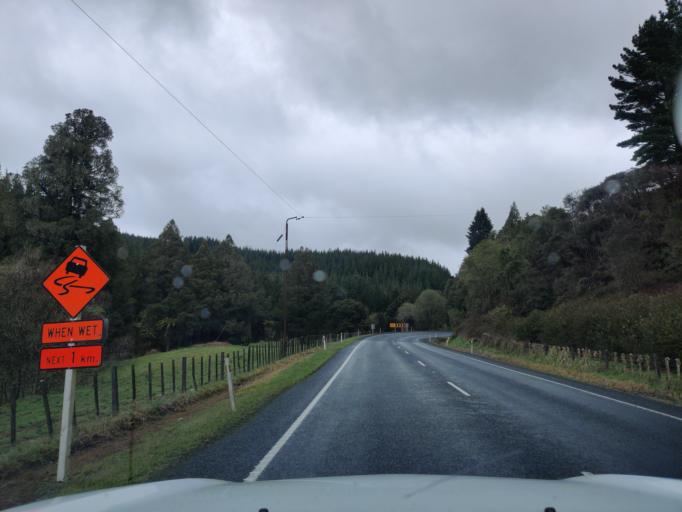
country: NZ
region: Waikato
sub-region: Otorohanga District
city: Otorohanga
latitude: -38.6566
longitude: 175.2084
